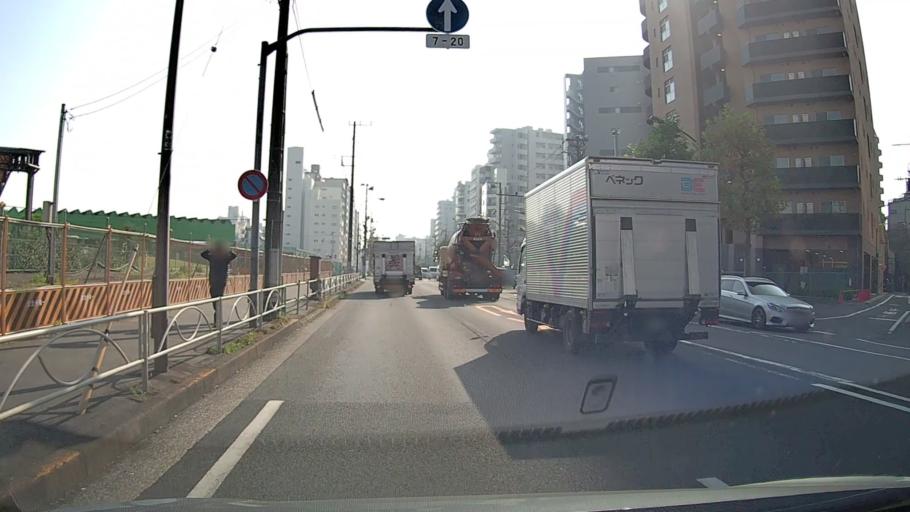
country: JP
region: Tokyo
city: Tokyo
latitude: 35.7382
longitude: 139.7338
